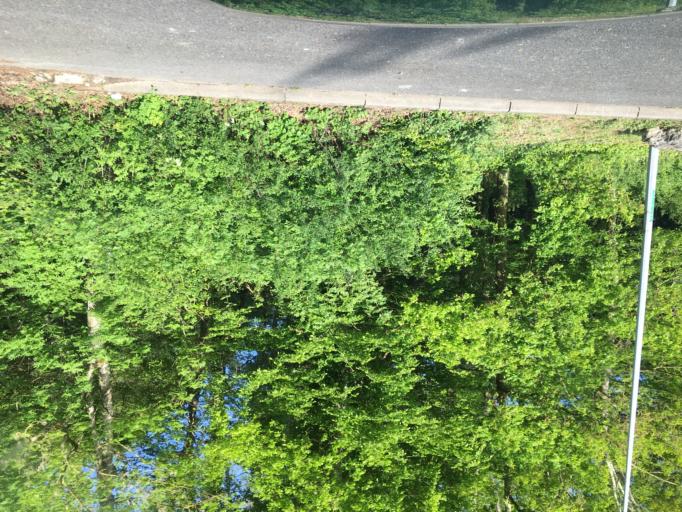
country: FR
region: Centre
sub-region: Departement du Loiret
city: Ormes
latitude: 47.9391
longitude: 1.8373
